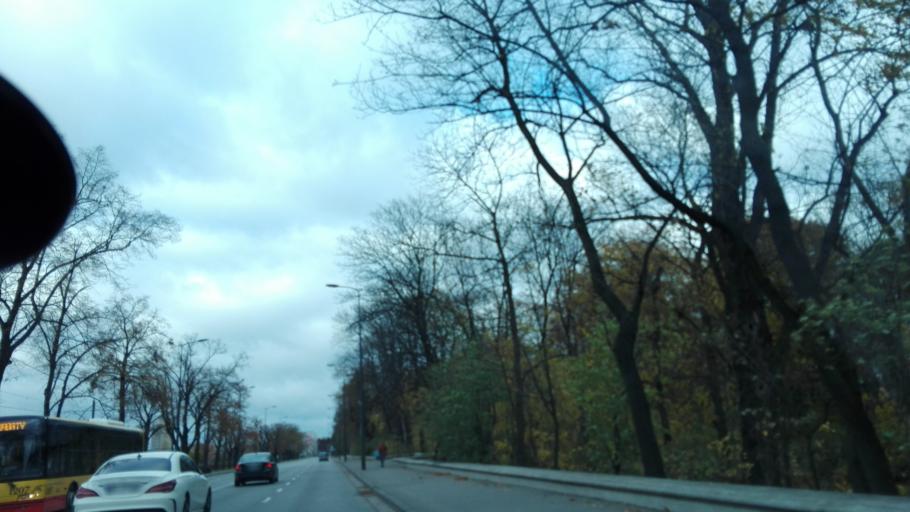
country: PL
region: Masovian Voivodeship
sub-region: Warszawa
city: Praga Polnoc
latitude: 52.2423
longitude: 21.0497
